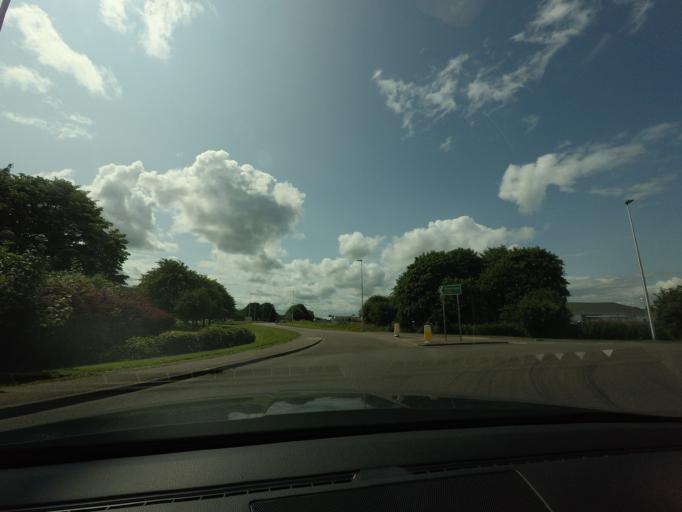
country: GB
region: Scotland
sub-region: Moray
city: Forres
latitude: 57.6074
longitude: -3.6298
